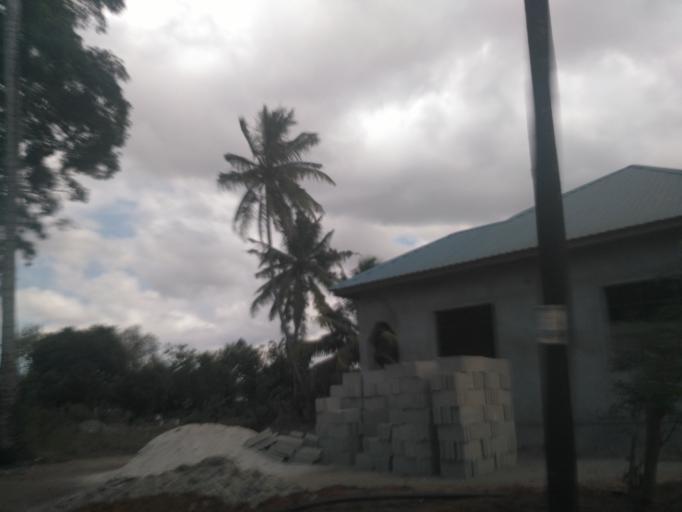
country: TZ
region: Dar es Salaam
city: Dar es Salaam
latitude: -6.8916
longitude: 39.2851
